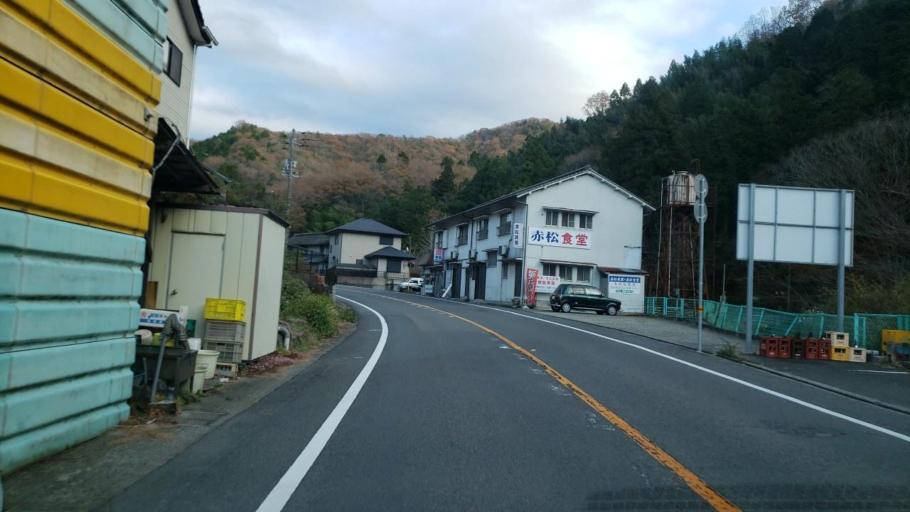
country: JP
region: Tokushima
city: Wakimachi
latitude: 34.1685
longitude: 134.0856
